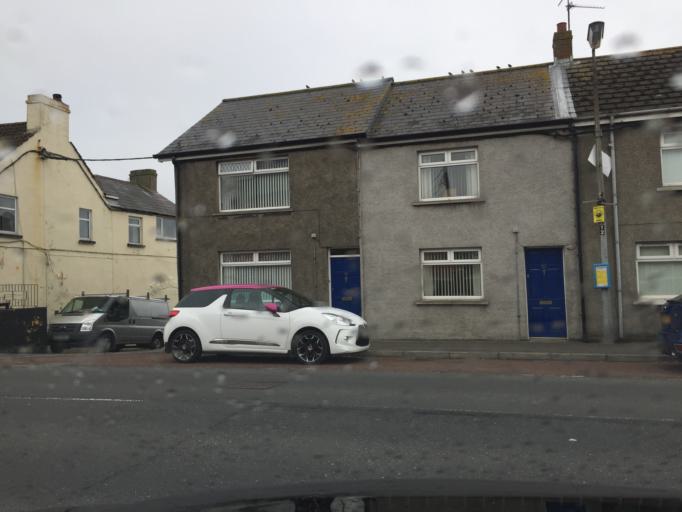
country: GB
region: Northern Ireland
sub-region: Down District
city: Kircubbin
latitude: 54.4875
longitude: -5.5330
